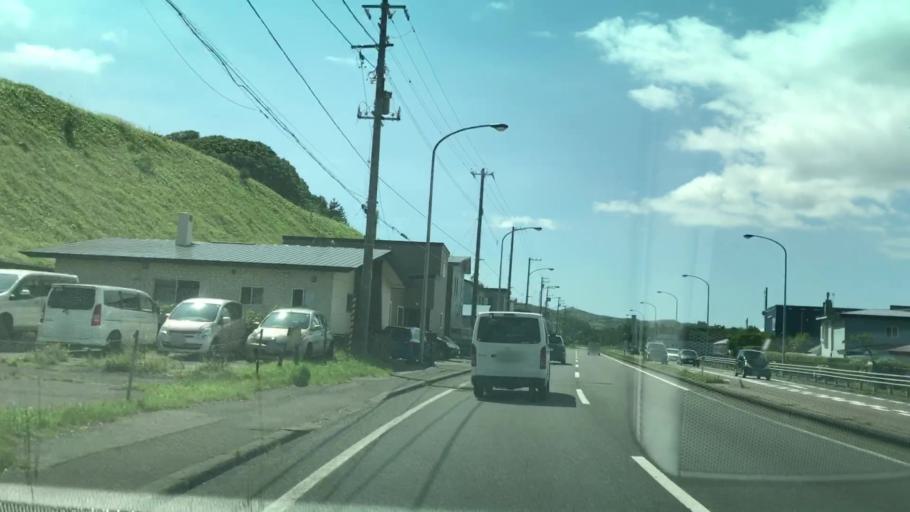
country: JP
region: Hokkaido
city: Muroran
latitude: 42.3501
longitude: 141.0420
